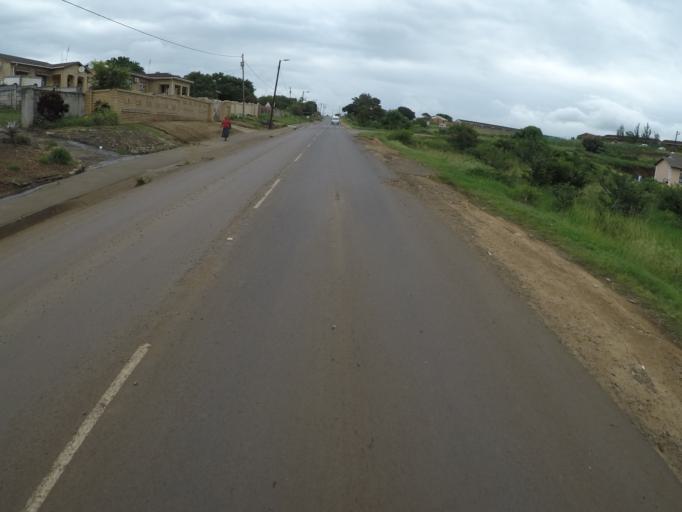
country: ZA
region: KwaZulu-Natal
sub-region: uThungulu District Municipality
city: Empangeni
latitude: -28.7829
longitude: 31.8589
